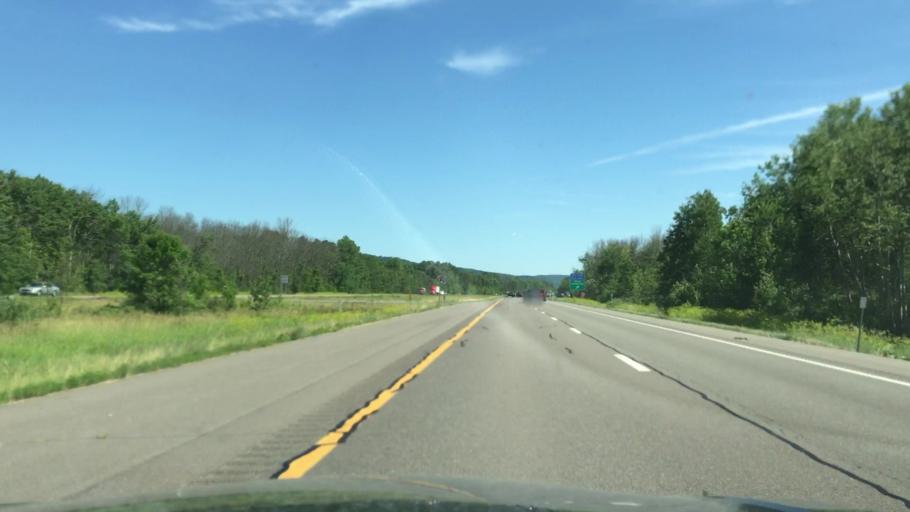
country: US
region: New York
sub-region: Steuben County
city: Gang Mills
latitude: 42.2487
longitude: -77.2028
